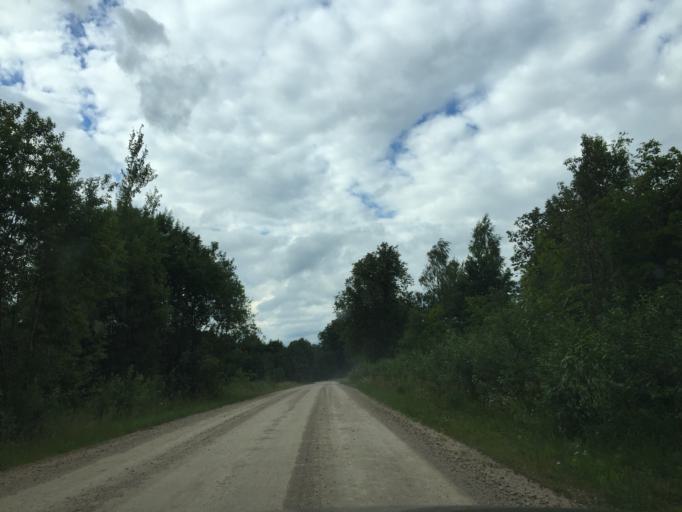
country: LV
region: Malpils
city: Malpils
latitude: 56.9608
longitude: 24.9848
